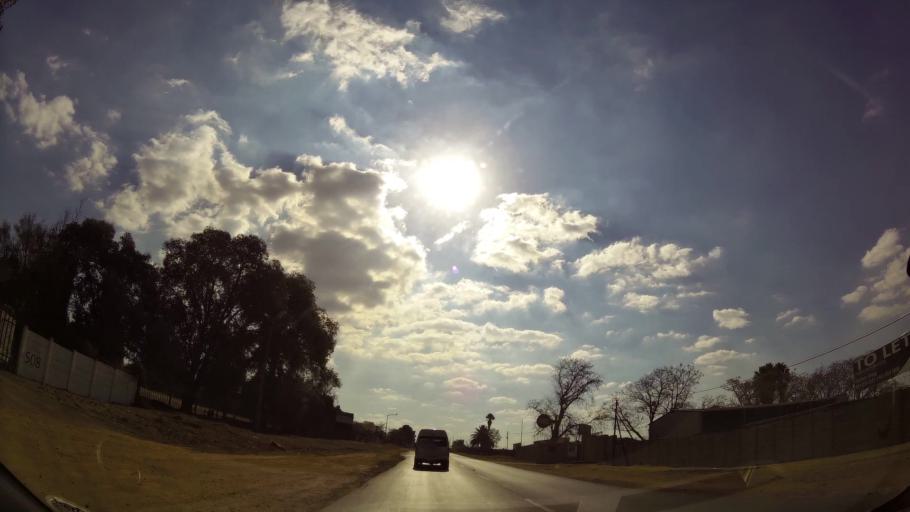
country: ZA
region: Gauteng
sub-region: Ekurhuleni Metropolitan Municipality
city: Benoni
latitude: -26.1307
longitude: 28.3534
